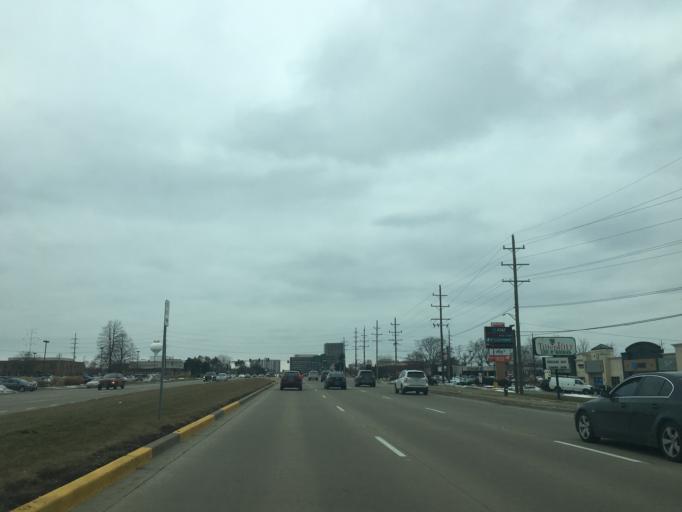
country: US
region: Illinois
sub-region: DuPage County
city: Oakbrook Terrace
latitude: 41.8464
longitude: -87.9692
